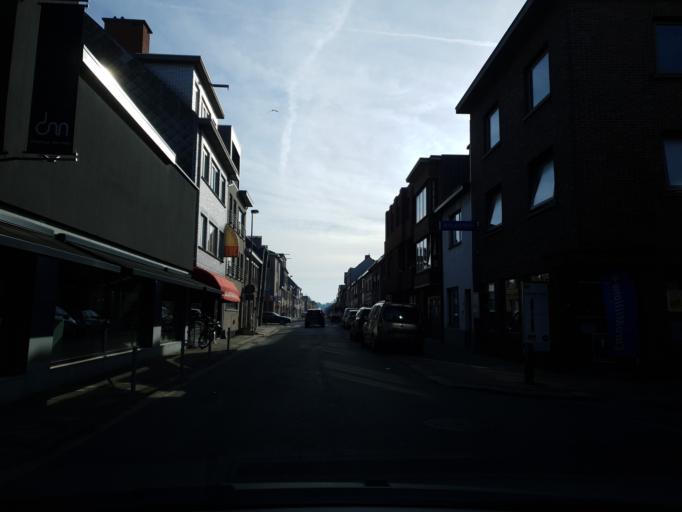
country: BE
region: Flanders
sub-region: Provincie Oost-Vlaanderen
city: Sint-Niklaas
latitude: 51.1599
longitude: 4.1567
